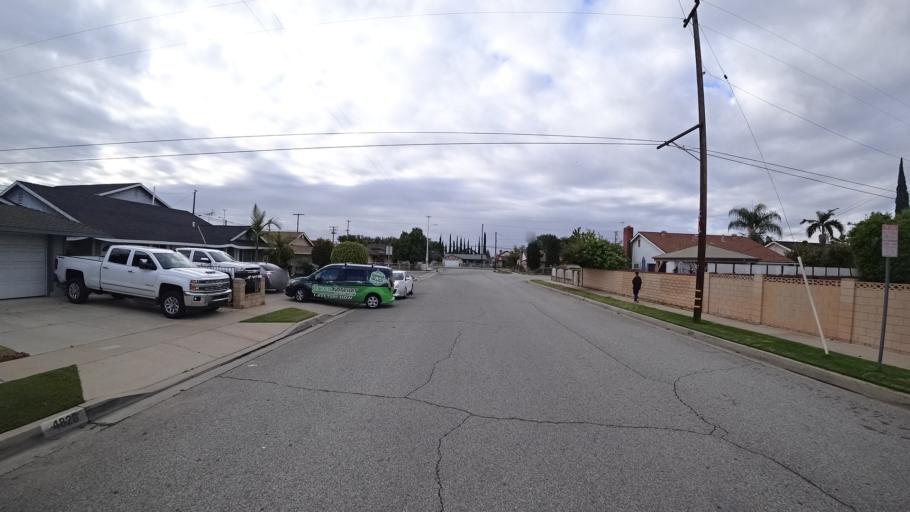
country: US
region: California
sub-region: Los Angeles County
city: Baldwin Park
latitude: 34.1004
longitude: -117.9720
